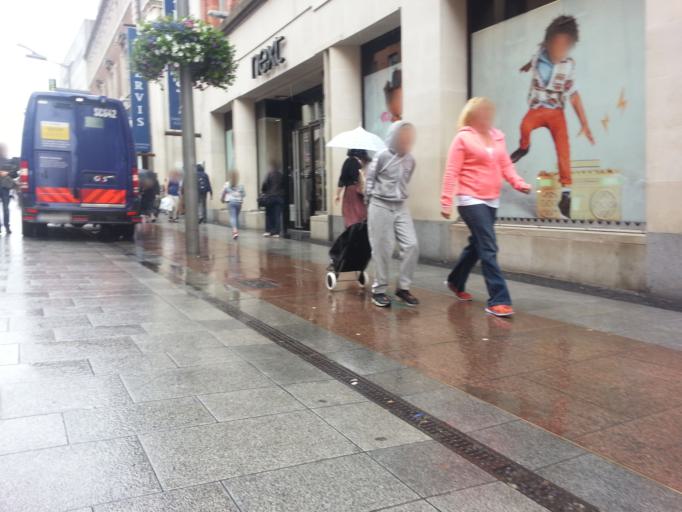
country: IE
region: Leinster
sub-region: Dublin City
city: Dublin
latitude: 53.3489
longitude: -6.2661
